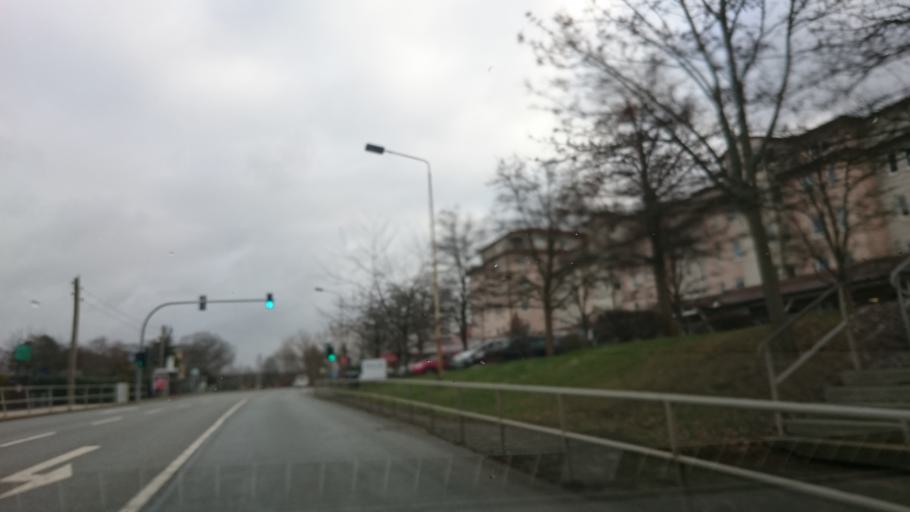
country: DE
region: Saxony
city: Werdau
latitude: 50.7357
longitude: 12.3878
